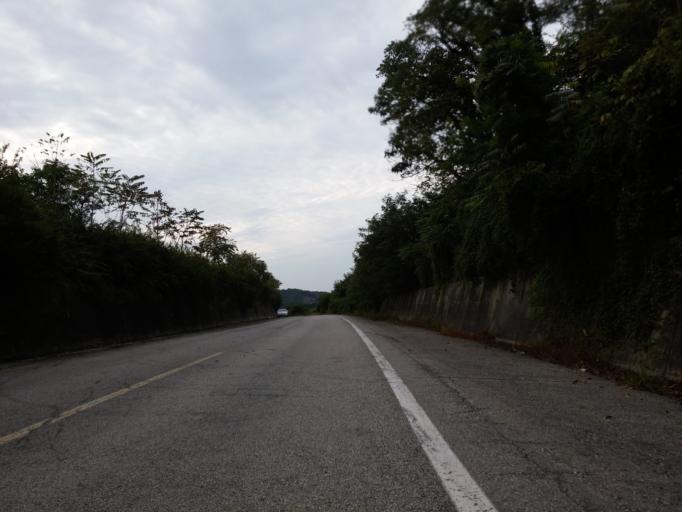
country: KR
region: Chungcheongnam-do
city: Yonmu
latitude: 36.1642
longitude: 127.1936
